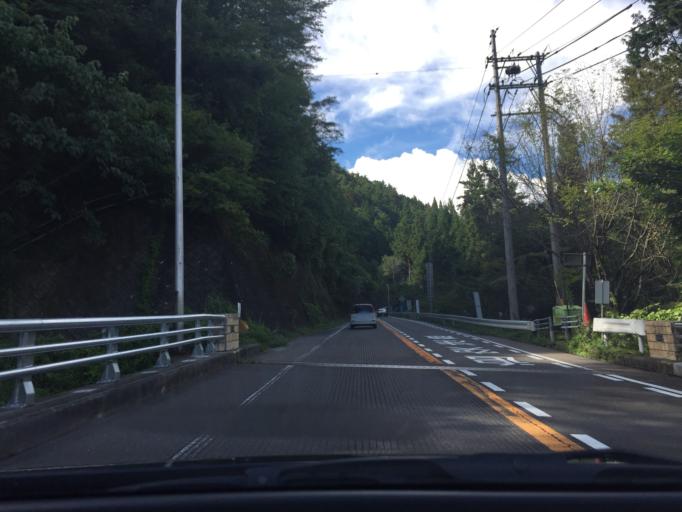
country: JP
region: Gifu
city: Nakatsugawa
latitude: 35.6780
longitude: 137.4121
